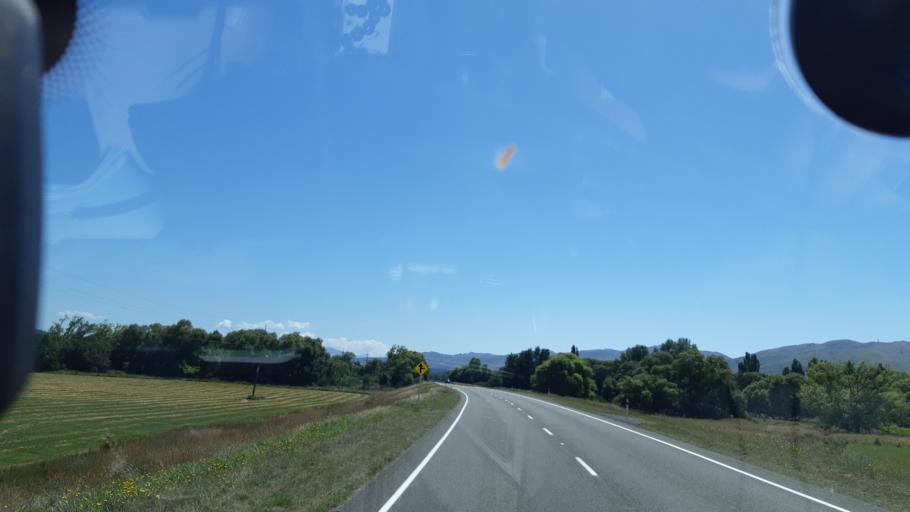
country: NZ
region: Canterbury
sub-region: Kaikoura District
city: Kaikoura
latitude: -42.7269
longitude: 173.2792
